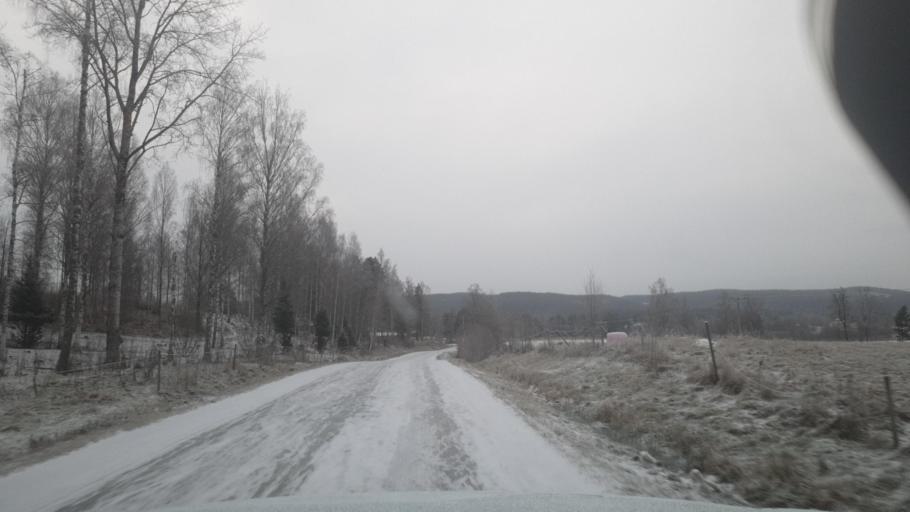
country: SE
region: Vaermland
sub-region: Arvika Kommun
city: Arvika
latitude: 59.5296
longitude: 12.8251
